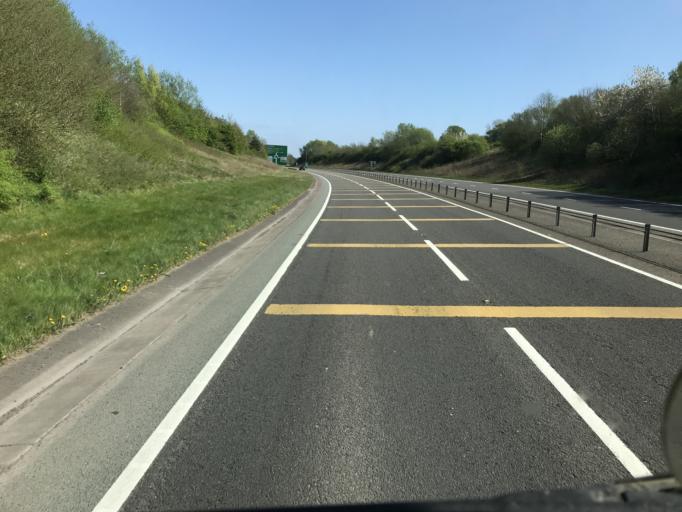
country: GB
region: England
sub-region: Cheshire East
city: Weston
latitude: 53.0691
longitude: -2.3897
